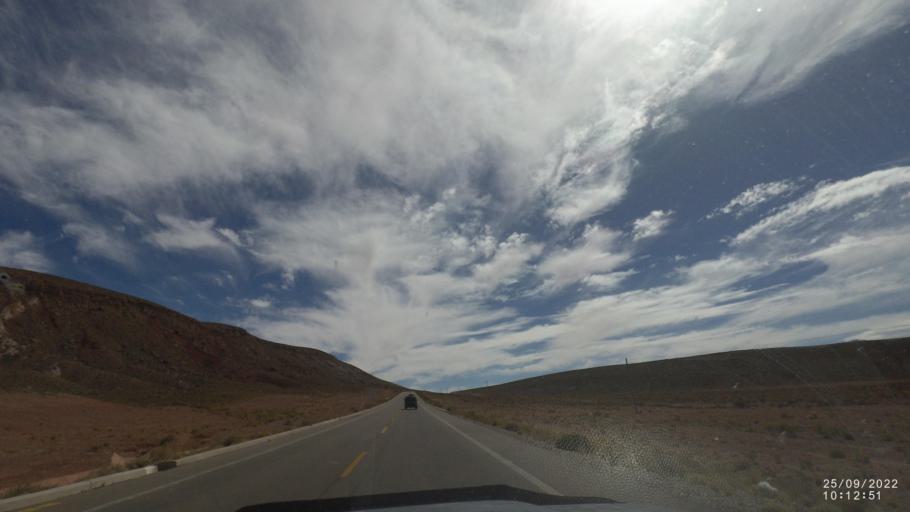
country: BO
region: Potosi
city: Colchani
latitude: -20.0809
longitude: -66.8907
